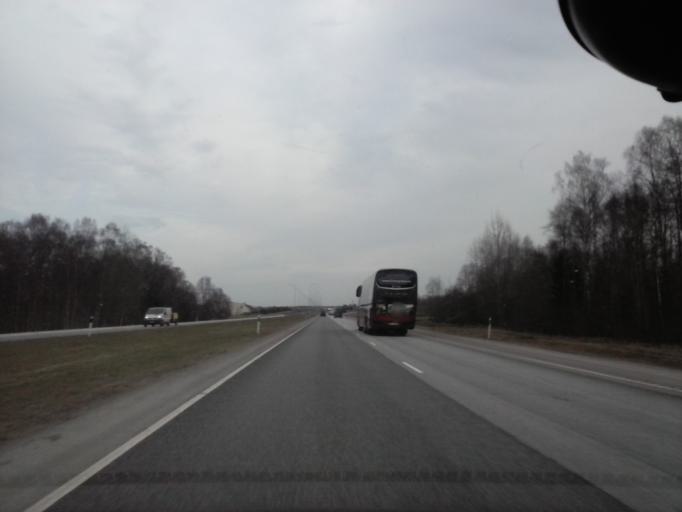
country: EE
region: Harju
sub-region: Rae vald
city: Vaida
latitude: 59.3188
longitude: 24.9278
